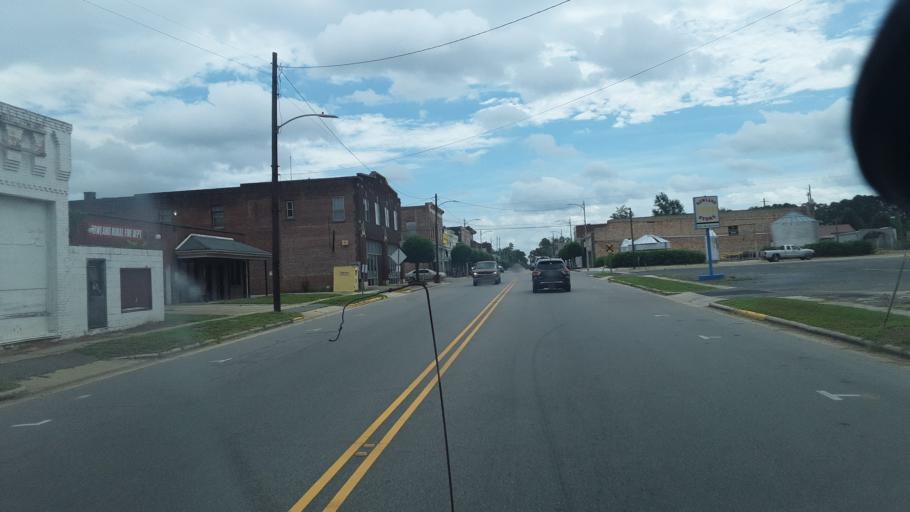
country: US
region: North Carolina
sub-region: Robeson County
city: Rowland
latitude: 34.5381
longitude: -79.2946
